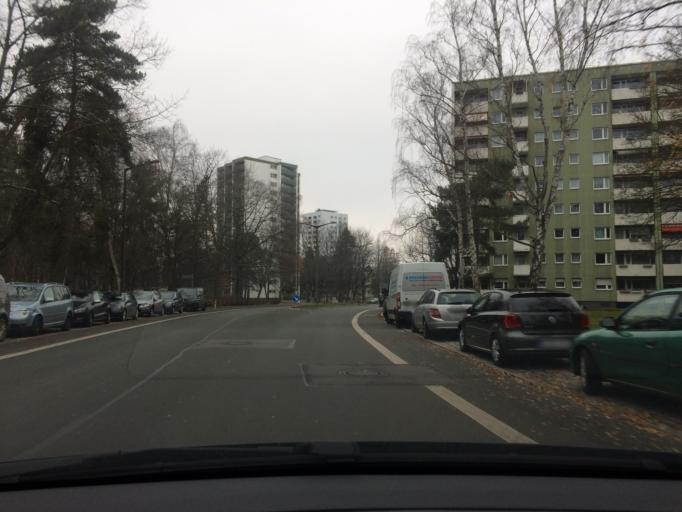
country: DE
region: Bavaria
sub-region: Regierungsbezirk Mittelfranken
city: Nuernberg
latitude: 49.4116
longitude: 11.1175
